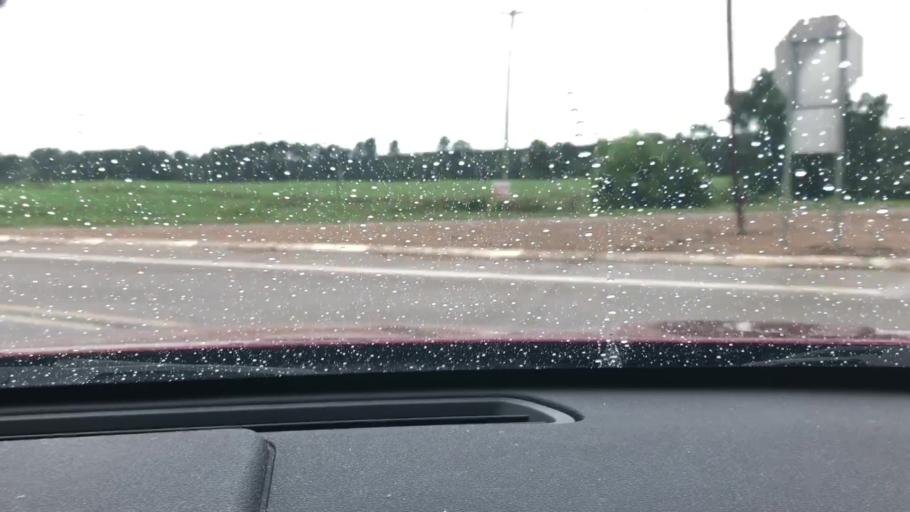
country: US
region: Arkansas
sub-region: Columbia County
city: Magnolia
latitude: 33.2973
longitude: -93.2361
